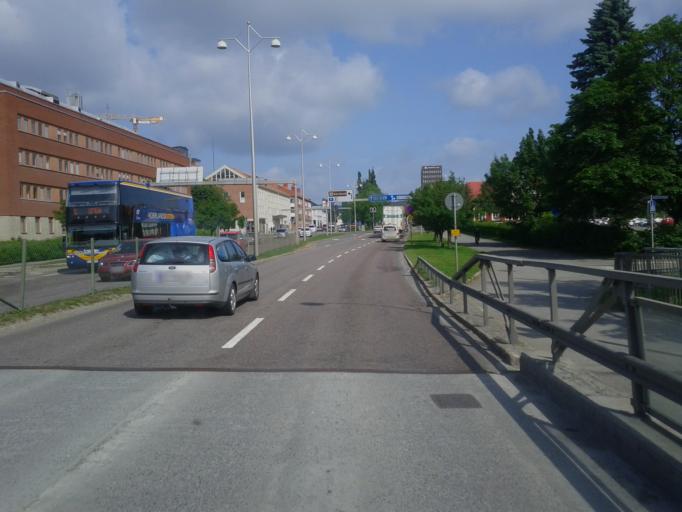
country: SE
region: Vaesterbotten
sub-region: Skelleftea Kommun
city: Skelleftea
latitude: 64.7480
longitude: 20.9601
